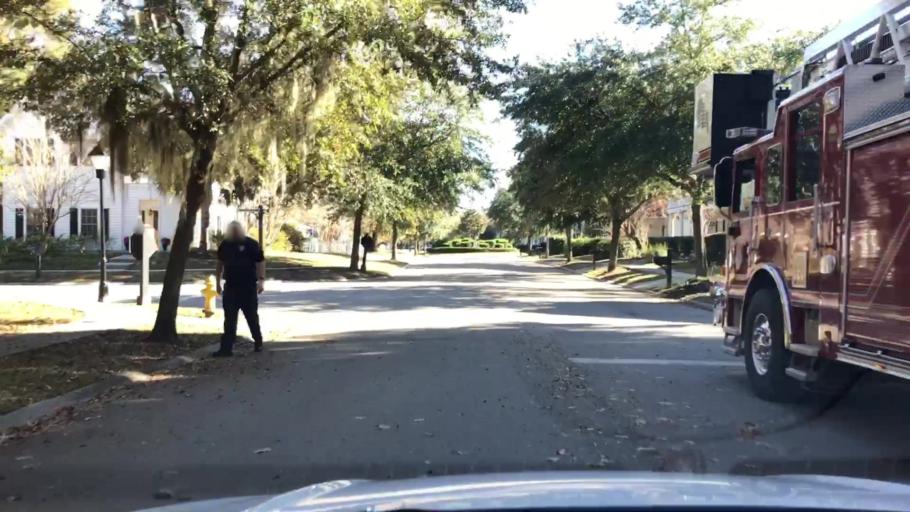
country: US
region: South Carolina
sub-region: Beaufort County
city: Bluffton
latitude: 32.2677
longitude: -80.8723
